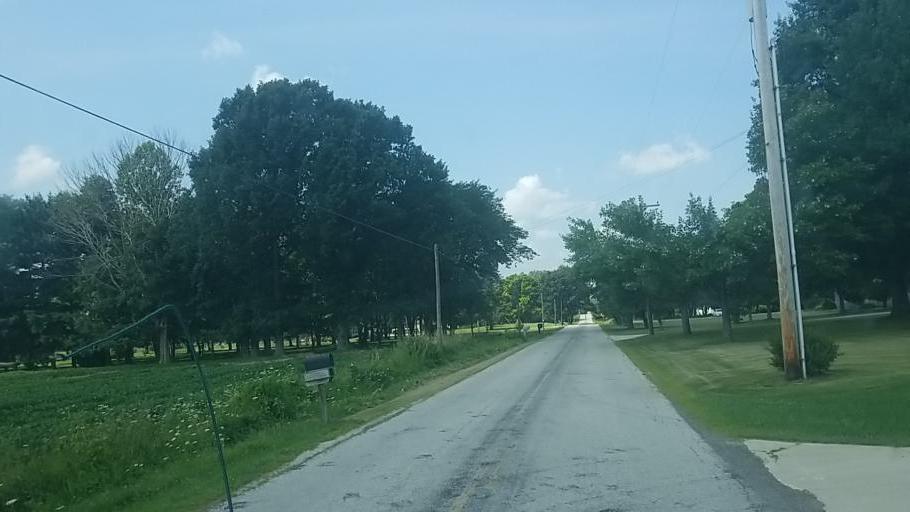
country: US
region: Ohio
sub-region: Crawford County
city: Crestline
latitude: 40.7986
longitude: -82.6660
